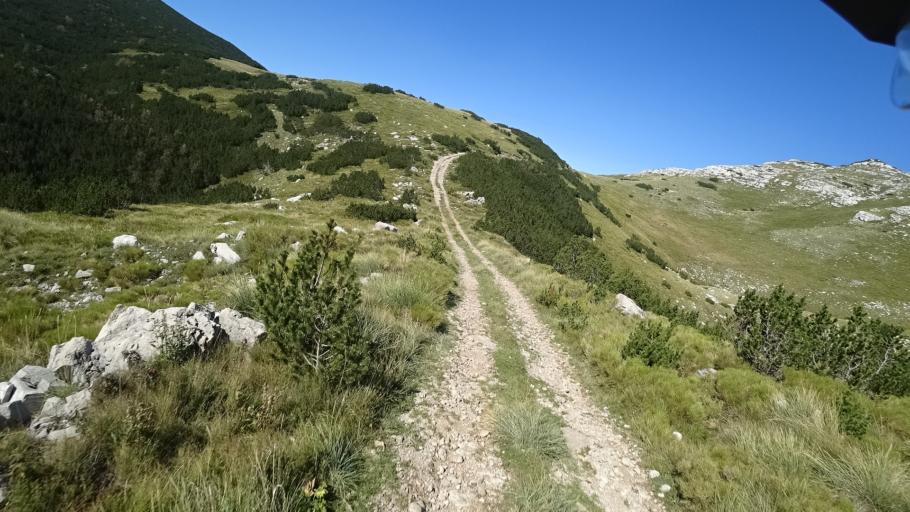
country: HR
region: Splitsko-Dalmatinska
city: Hrvace
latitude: 43.9385
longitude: 16.5882
